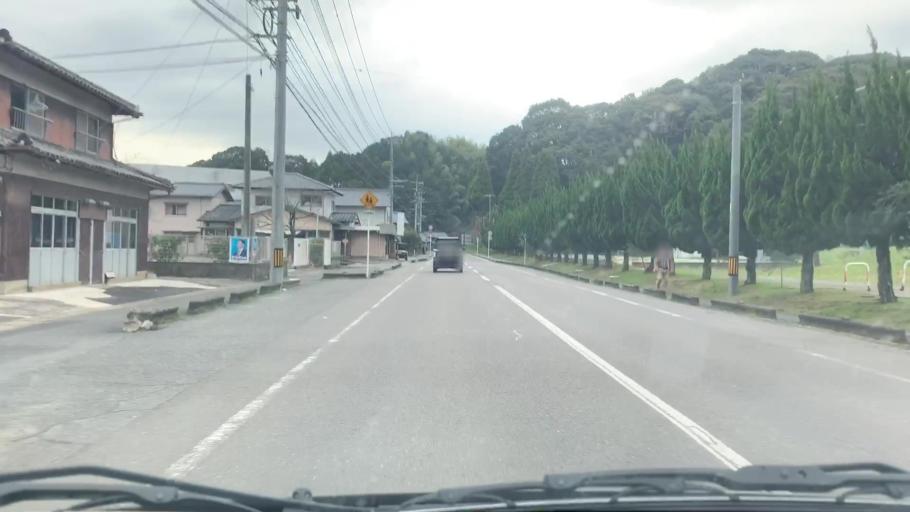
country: JP
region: Saga Prefecture
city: Takeocho-takeo
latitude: 33.1929
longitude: 130.0312
